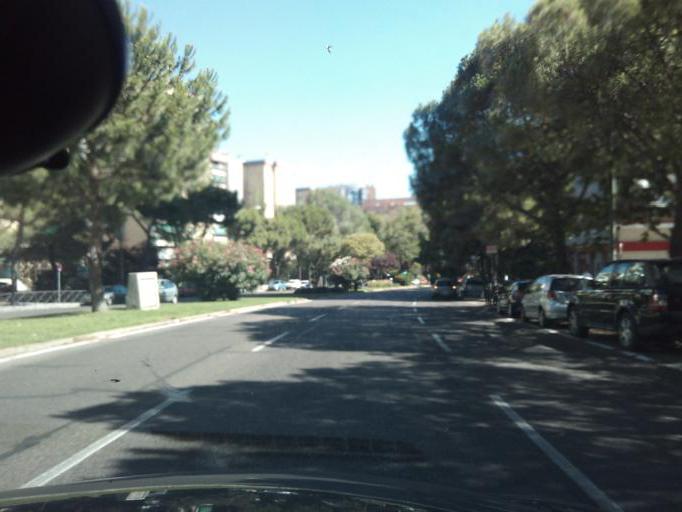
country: ES
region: Madrid
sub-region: Provincia de Madrid
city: Pinar de Chamartin
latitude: 40.4779
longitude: -3.6686
